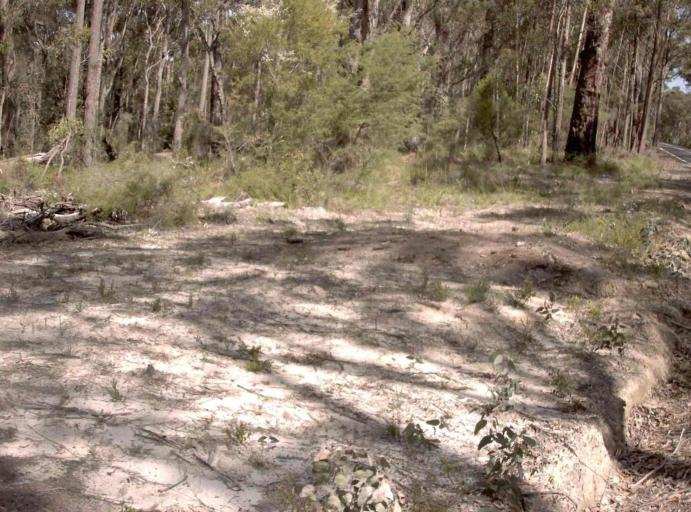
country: AU
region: New South Wales
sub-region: Bega Valley
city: Eden
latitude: -37.5388
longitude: 149.6962
